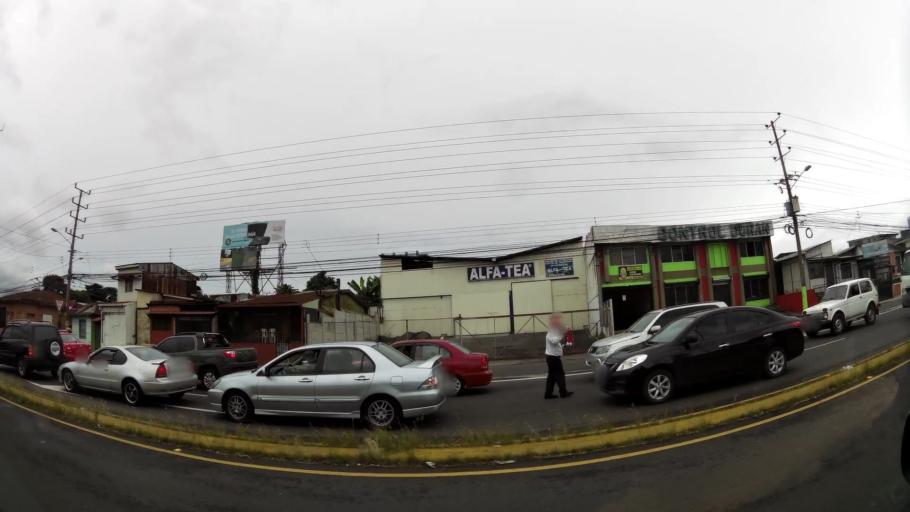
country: CR
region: San Jose
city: Calle Blancos
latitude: 9.9466
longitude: -84.0623
